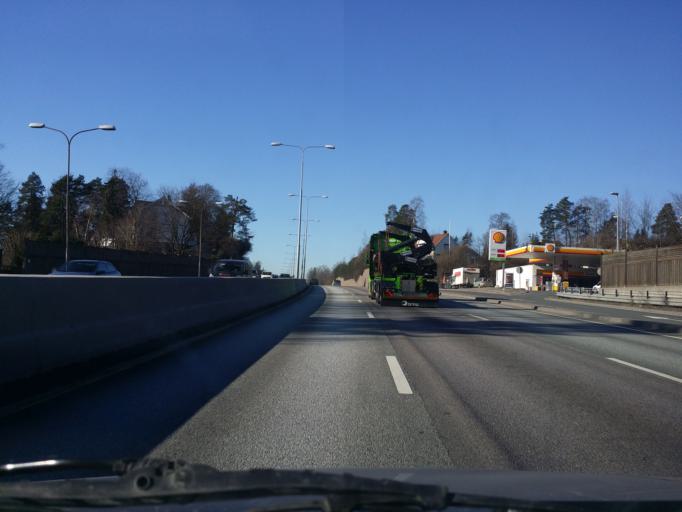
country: NO
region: Akershus
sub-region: Baerum
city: Lysaker
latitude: 59.9046
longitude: 10.6029
